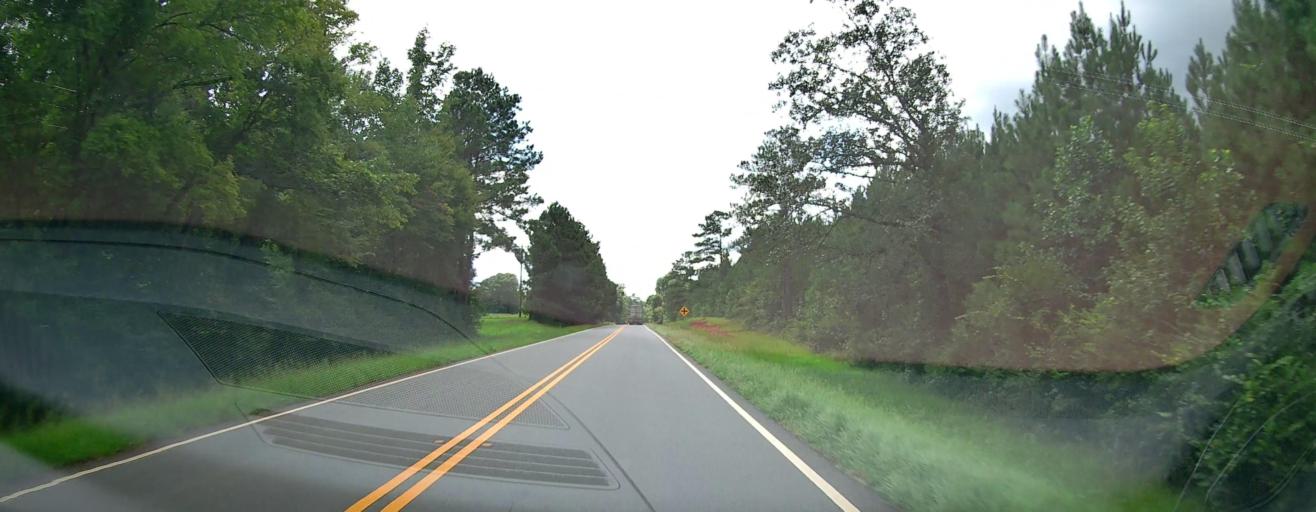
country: US
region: Georgia
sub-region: Bibb County
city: West Point
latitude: 32.8652
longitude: -83.8884
